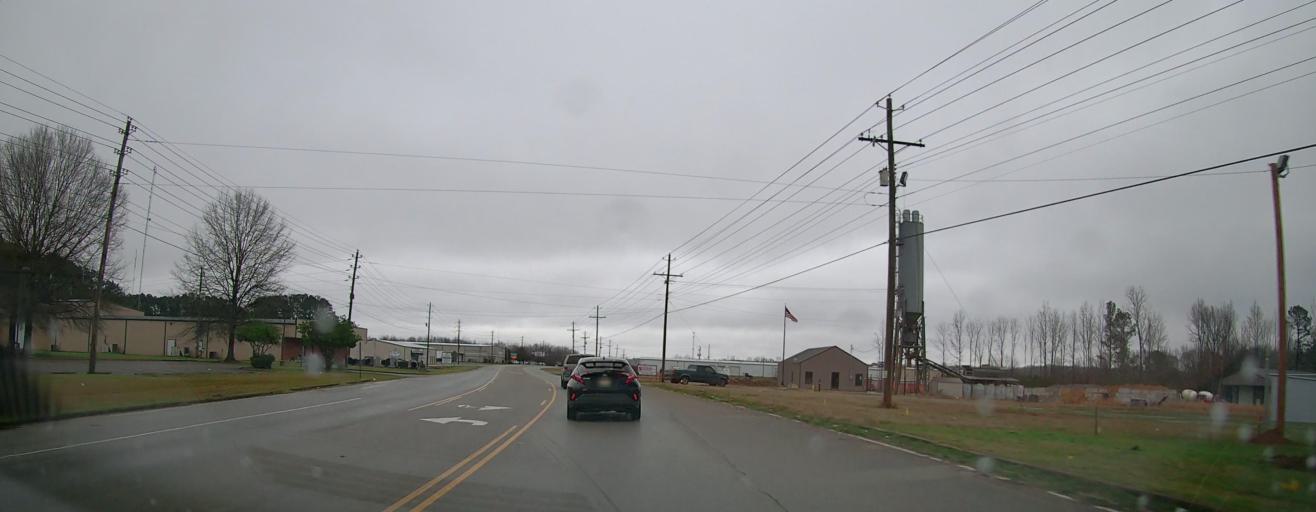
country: US
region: Mississippi
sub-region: Alcorn County
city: Corinth
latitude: 34.9087
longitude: -88.5228
